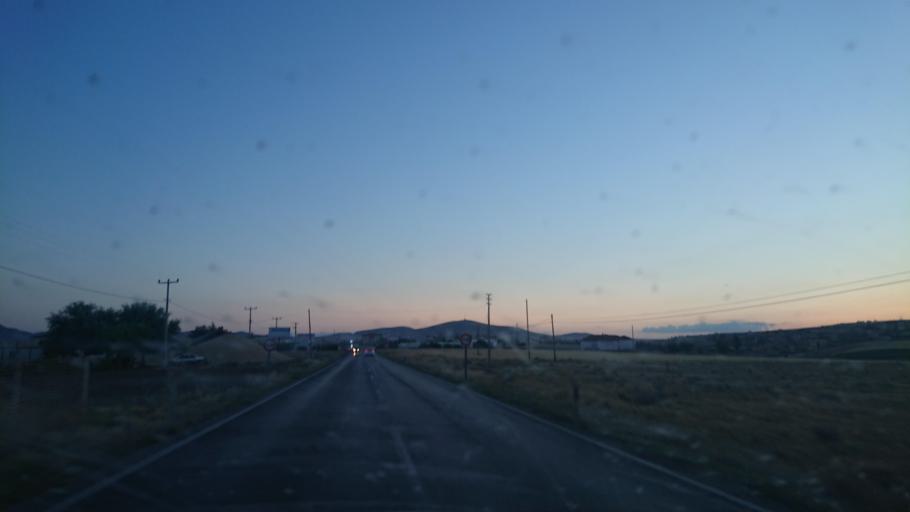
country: TR
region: Aksaray
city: Balci
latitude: 38.7604
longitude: 34.0841
